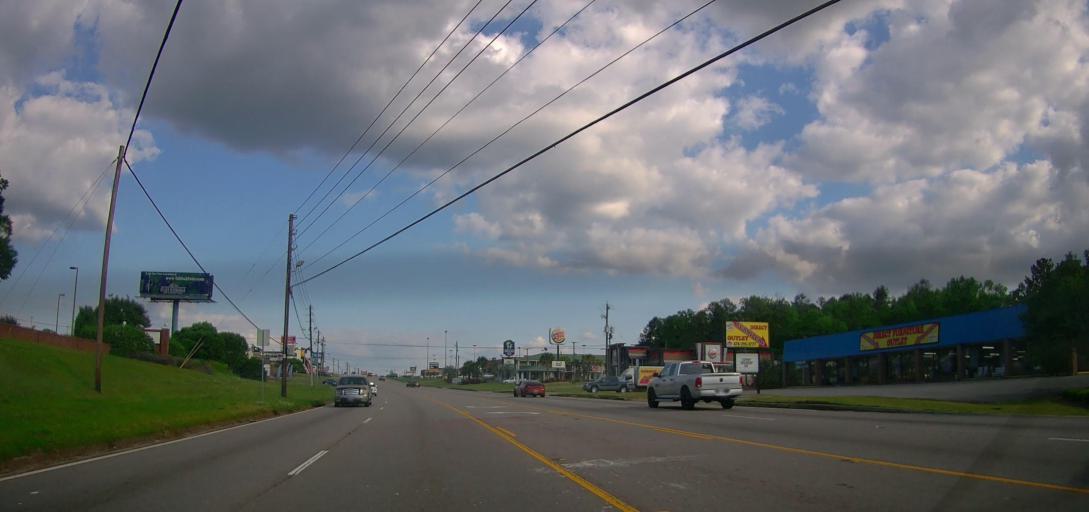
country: US
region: Georgia
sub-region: Baldwin County
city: Milledgeville
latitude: 33.1132
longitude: -83.2589
